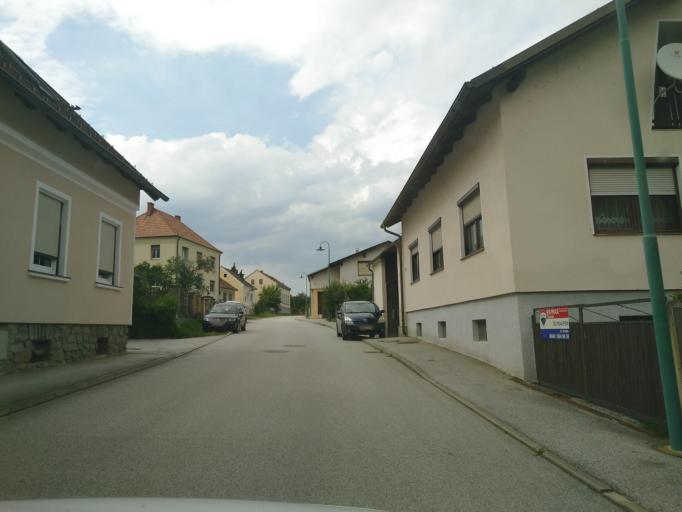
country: AT
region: Burgenland
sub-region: Politischer Bezirk Oberwart
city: Oberschutzen
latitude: 47.3485
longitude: 16.2057
